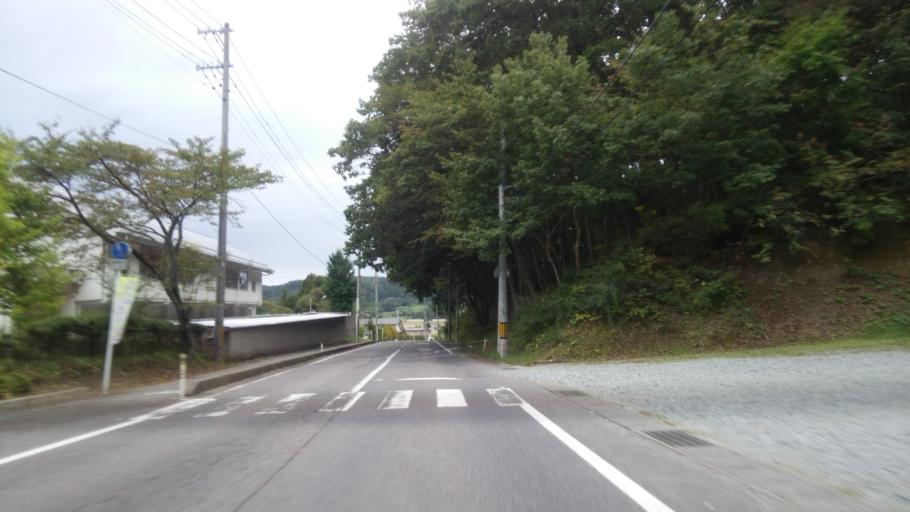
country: JP
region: Fukushima
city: Sukagawa
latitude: 37.2586
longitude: 140.2485
